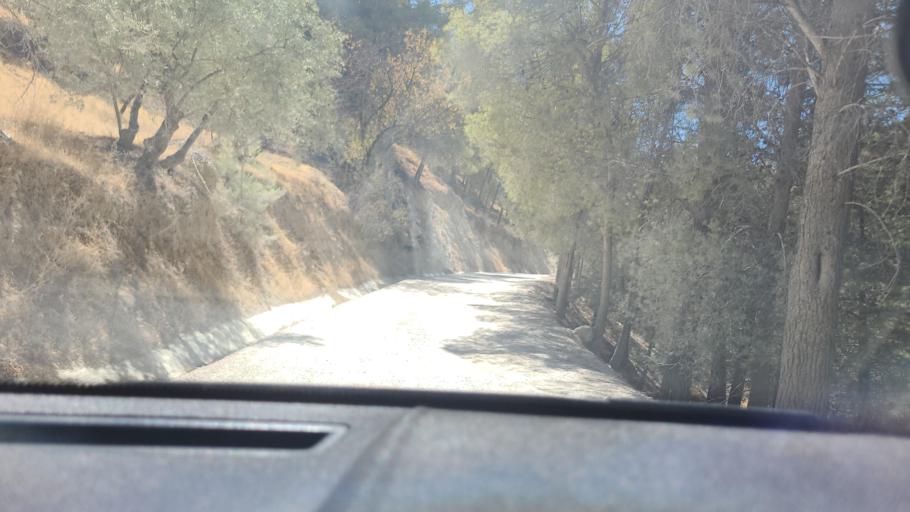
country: ES
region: Andalusia
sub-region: Provincia de Jaen
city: Belmez de la Moraleda
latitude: 37.7904
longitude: -3.4067
